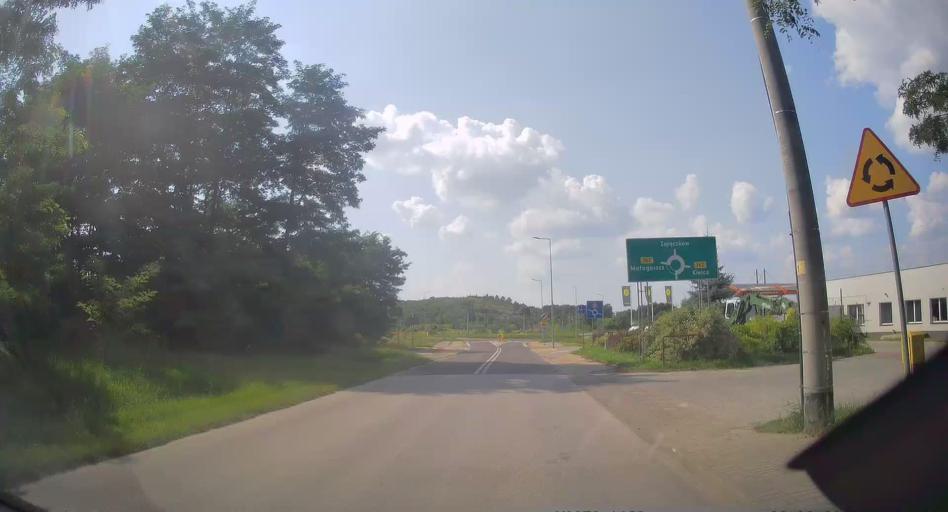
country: PL
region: Swietokrzyskie
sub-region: Powiat kielecki
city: Checiny
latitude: 50.8040
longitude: 20.4481
